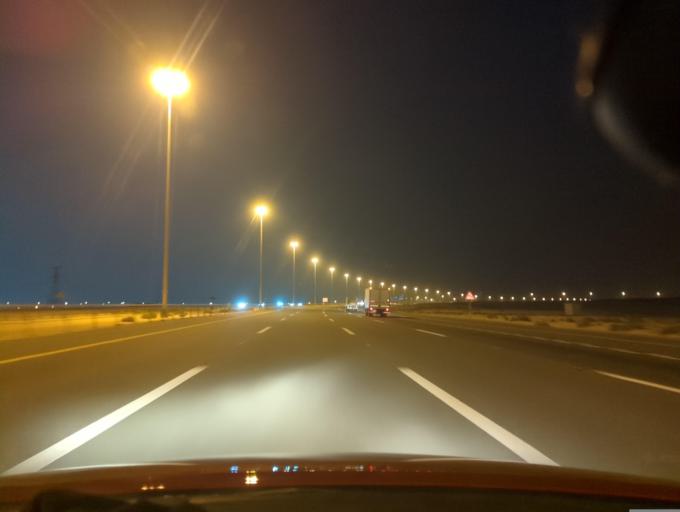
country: AE
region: Abu Dhabi
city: Abu Dhabi
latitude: 24.4458
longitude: 54.7552
